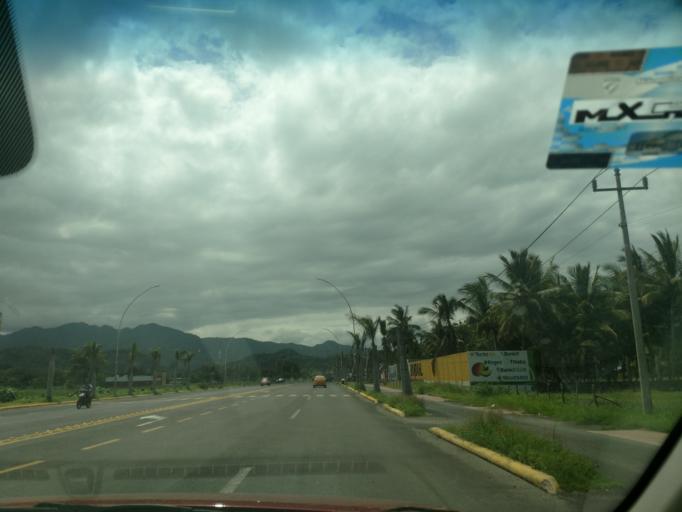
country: MX
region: Nayarit
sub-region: San Blas
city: Aticama
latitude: 21.5060
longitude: -105.2076
